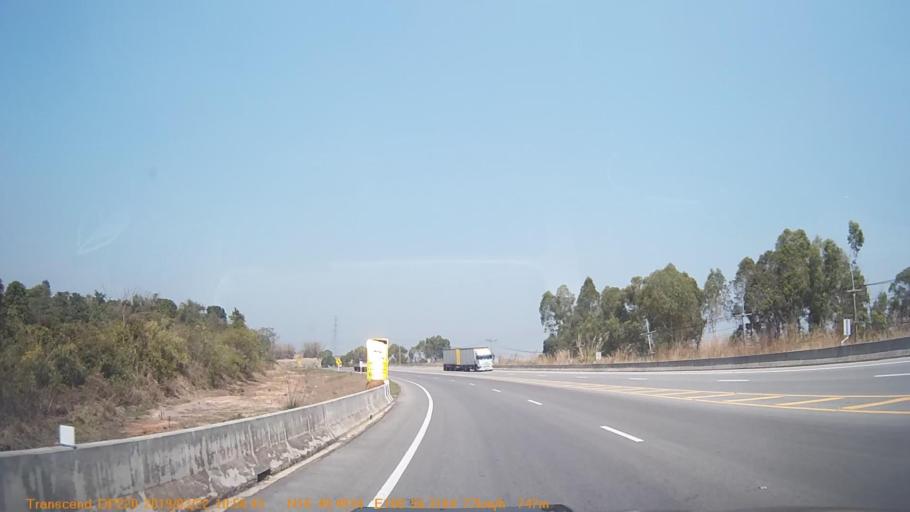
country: TH
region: Phetchabun
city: Khao Kho
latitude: 16.8250
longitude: 100.9385
